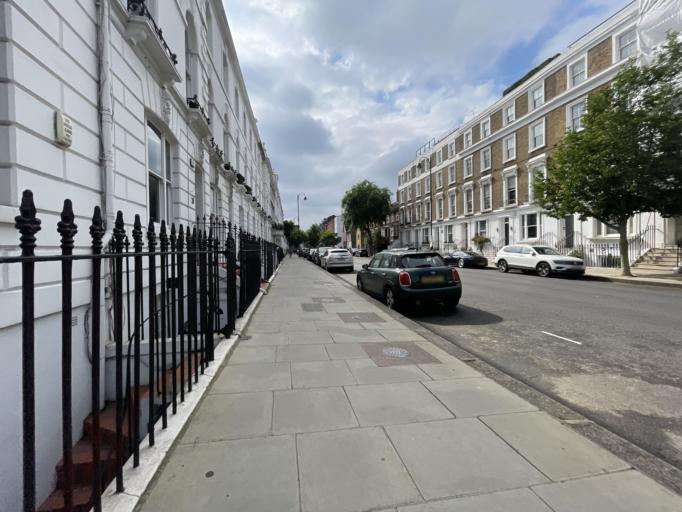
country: GB
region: England
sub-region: Greater London
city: Chelsea
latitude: 51.4859
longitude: -0.1690
